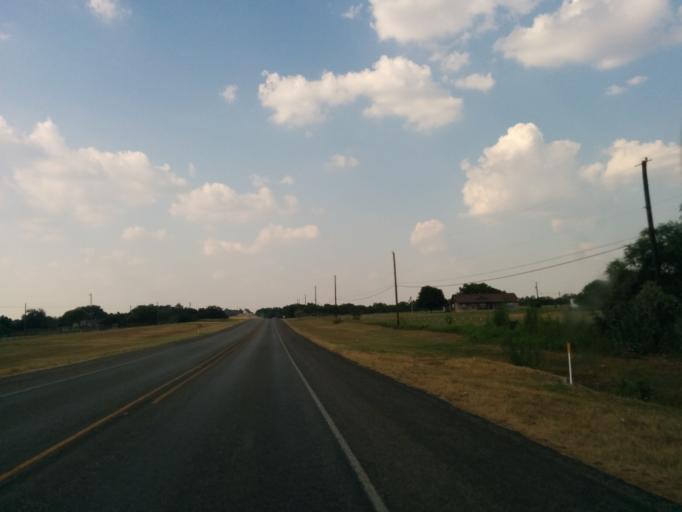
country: US
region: Texas
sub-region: Bexar County
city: Saint Hedwig
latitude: 29.3406
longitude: -98.2516
